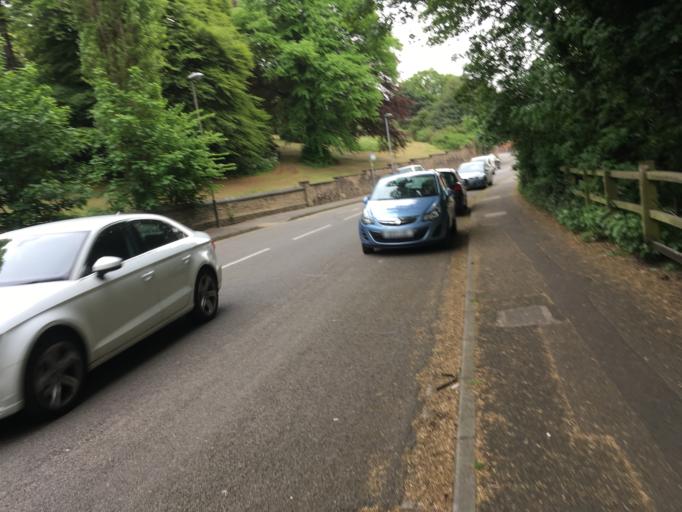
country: GB
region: England
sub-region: Derbyshire
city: Chesterfield
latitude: 53.2328
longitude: -1.4183
